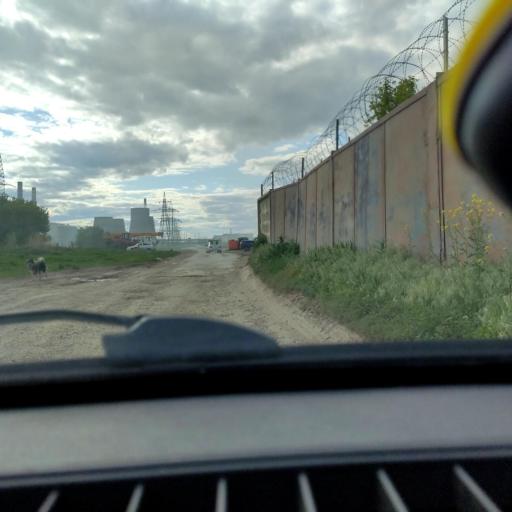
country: RU
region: Samara
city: Tol'yatti
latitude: 53.5463
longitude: 49.4742
